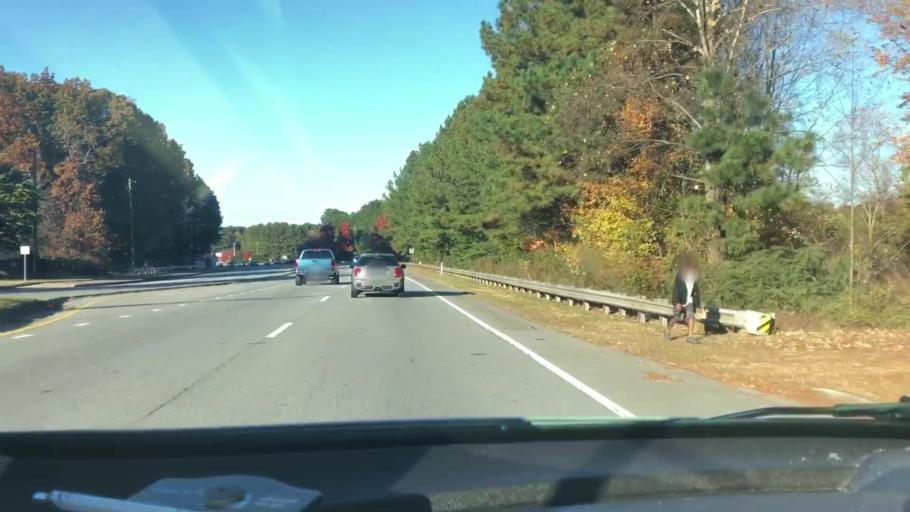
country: US
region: Georgia
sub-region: Gwinnett County
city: Berkeley Lake
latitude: 33.9940
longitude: -84.1681
